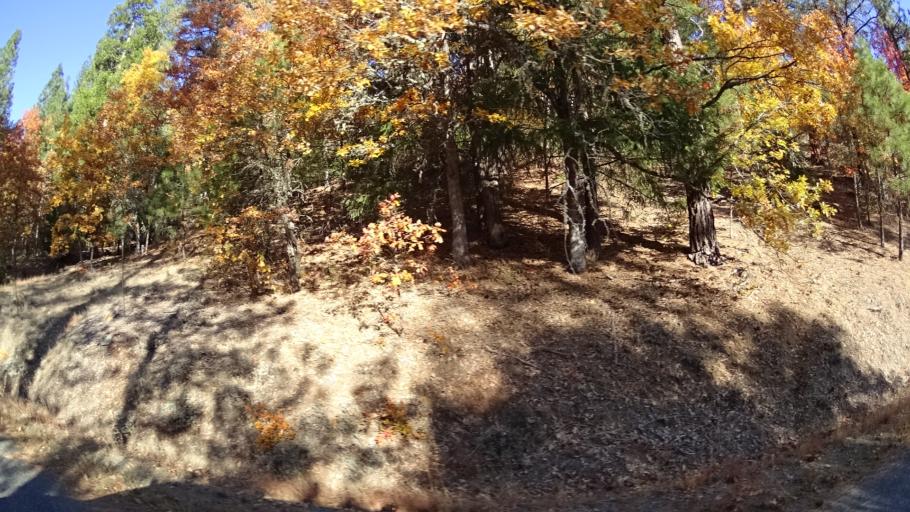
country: US
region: California
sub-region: Siskiyou County
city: Yreka
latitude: 41.6412
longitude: -123.0013
